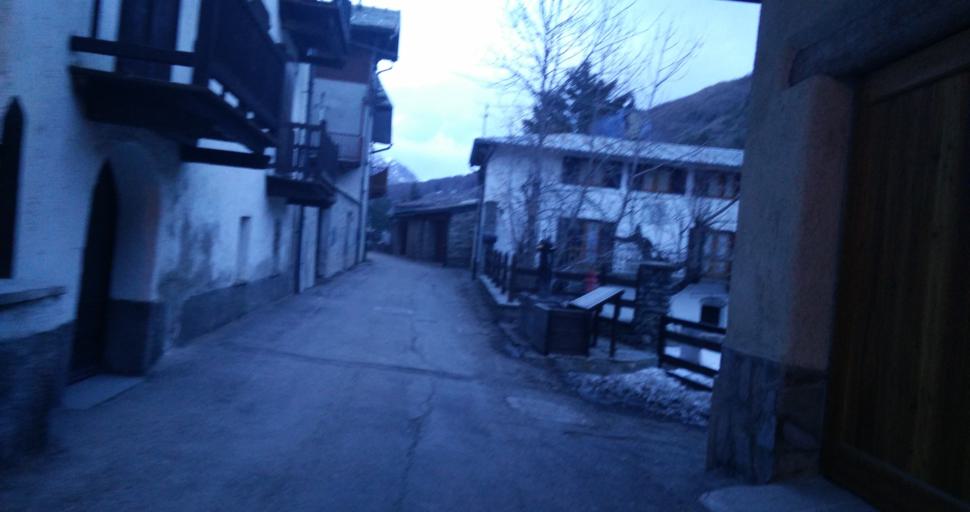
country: IT
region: Piedmont
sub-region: Provincia di Torino
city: Pragelato-Rua
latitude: 45.0107
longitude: 6.9392
